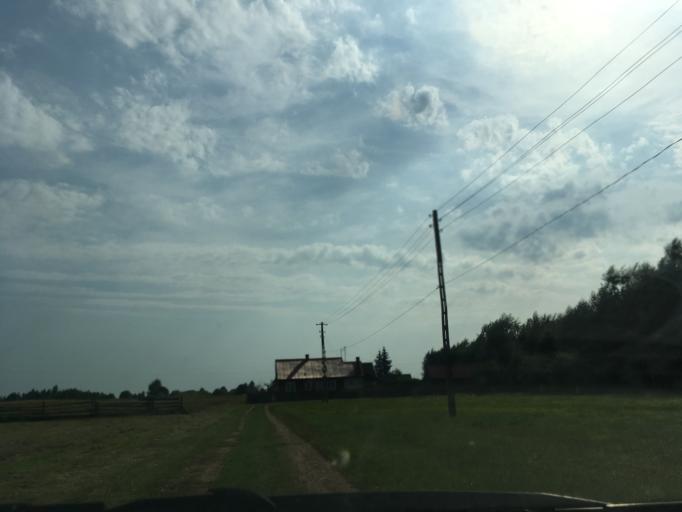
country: PL
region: Podlasie
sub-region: Powiat hajnowski
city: Bialowieza
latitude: 52.8959
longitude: 23.8337
